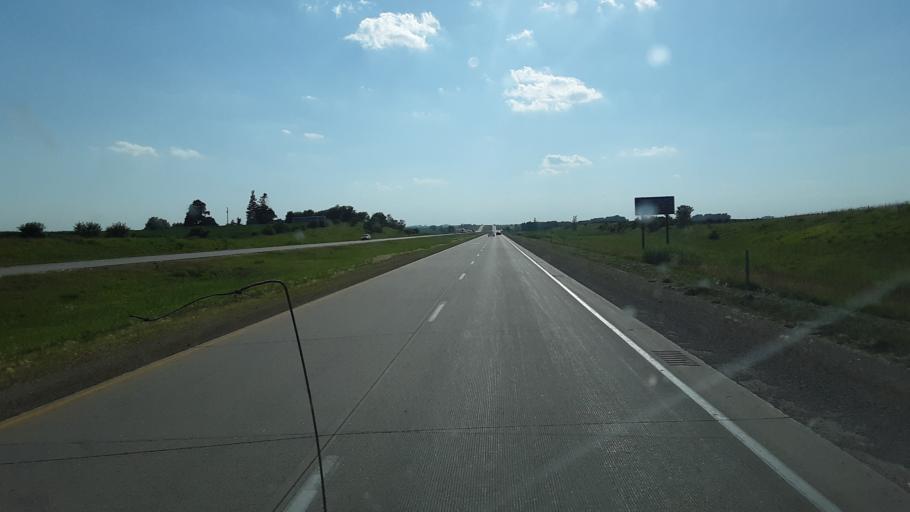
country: US
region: Iowa
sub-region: Grundy County
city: Grundy Center
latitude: 42.4631
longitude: -92.7451
